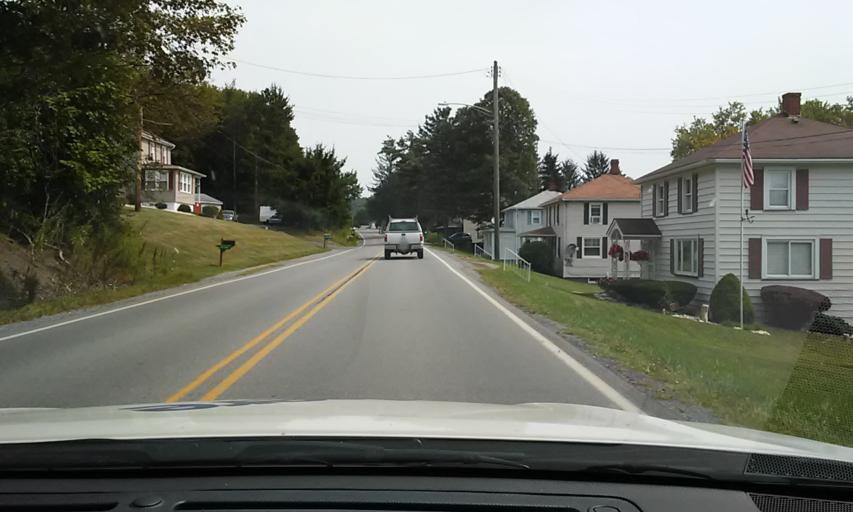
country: US
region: Pennsylvania
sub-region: Elk County
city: Saint Marys
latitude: 41.3204
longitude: -78.6390
